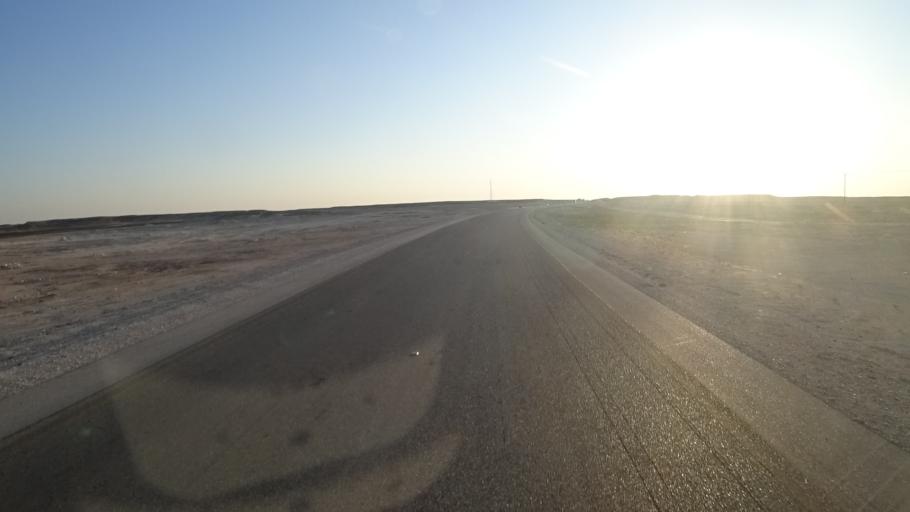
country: OM
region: Zufar
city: Salalah
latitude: 17.5447
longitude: 53.4222
